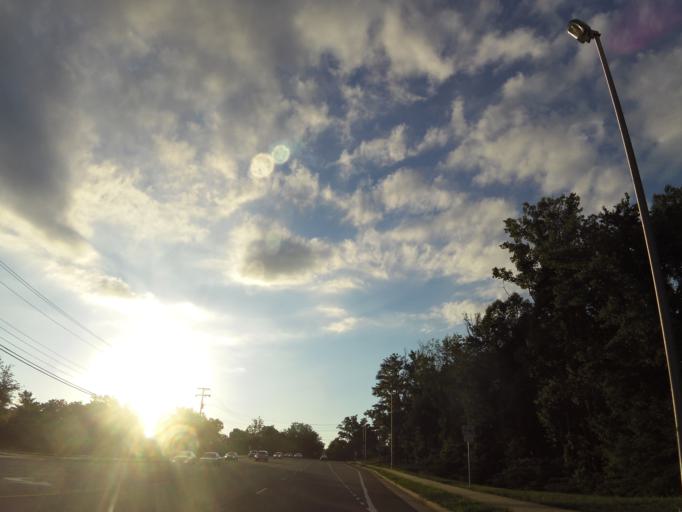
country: US
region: Tennessee
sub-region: Knox County
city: Farragut
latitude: 35.8908
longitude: -84.1708
